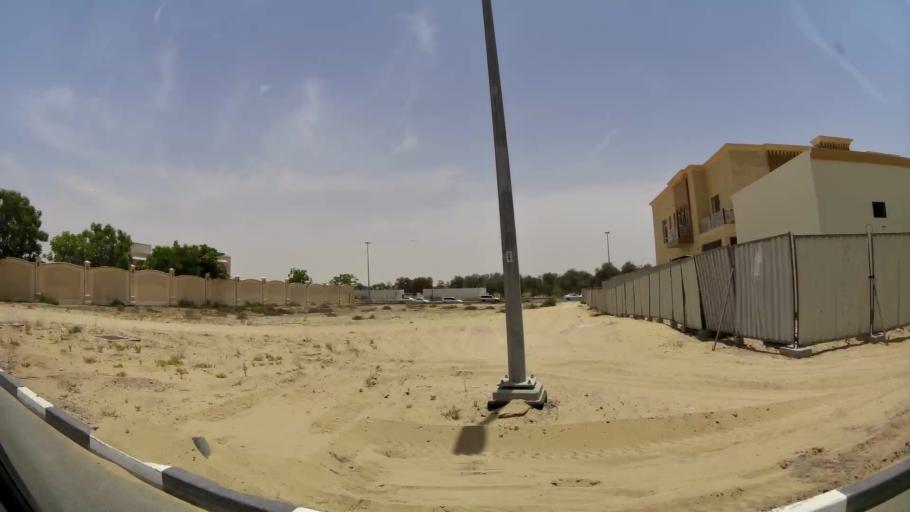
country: AE
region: Ash Shariqah
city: Sharjah
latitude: 25.2305
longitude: 55.4591
